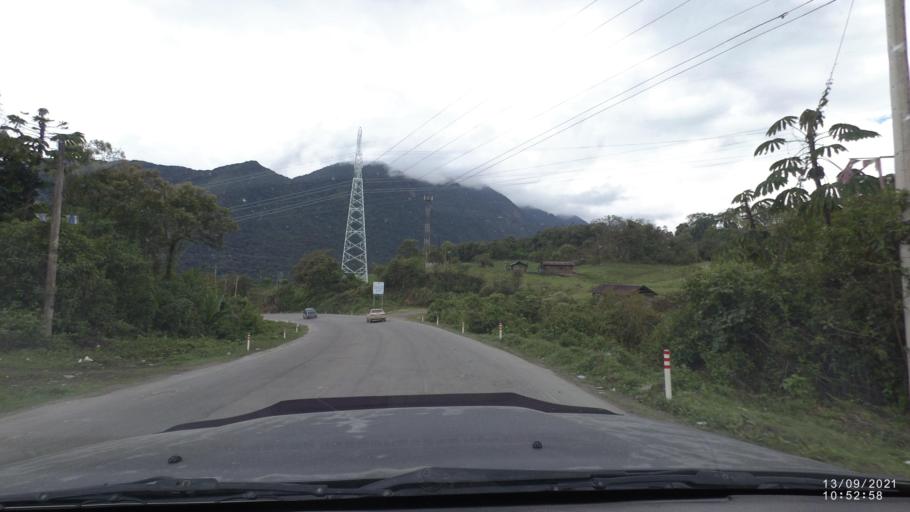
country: BO
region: Cochabamba
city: Colomi
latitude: -17.2018
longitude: -65.8322
